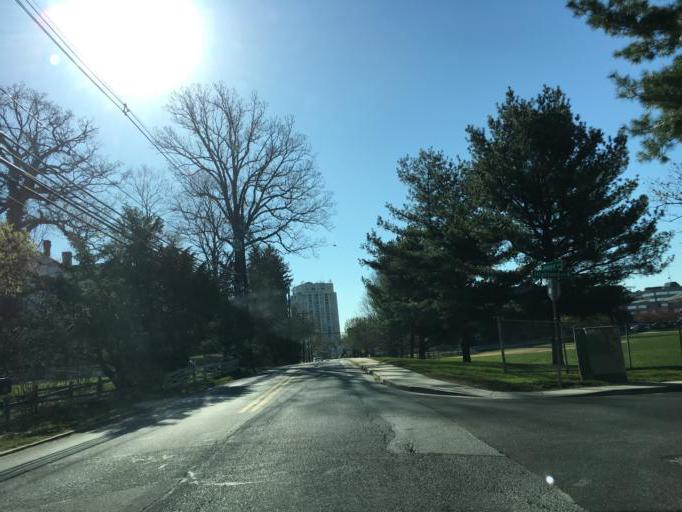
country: US
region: Maryland
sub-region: Baltimore County
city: Towson
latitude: 39.4049
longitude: -76.6108
